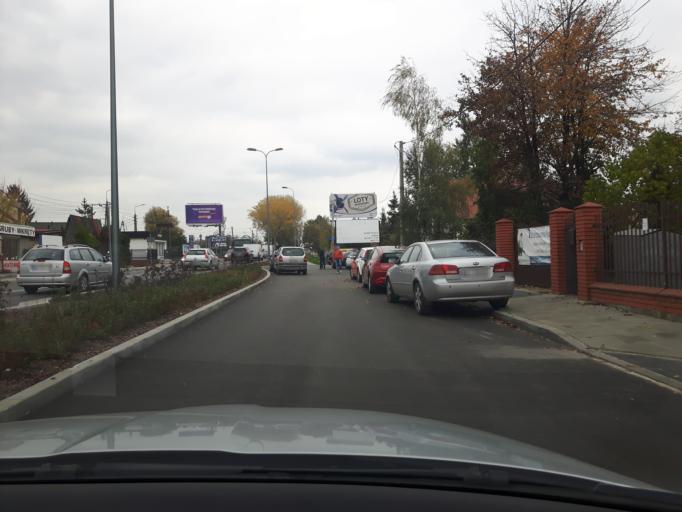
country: PL
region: Masovian Voivodeship
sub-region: Powiat wolominski
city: Zabki
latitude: 52.2860
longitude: 21.0967
